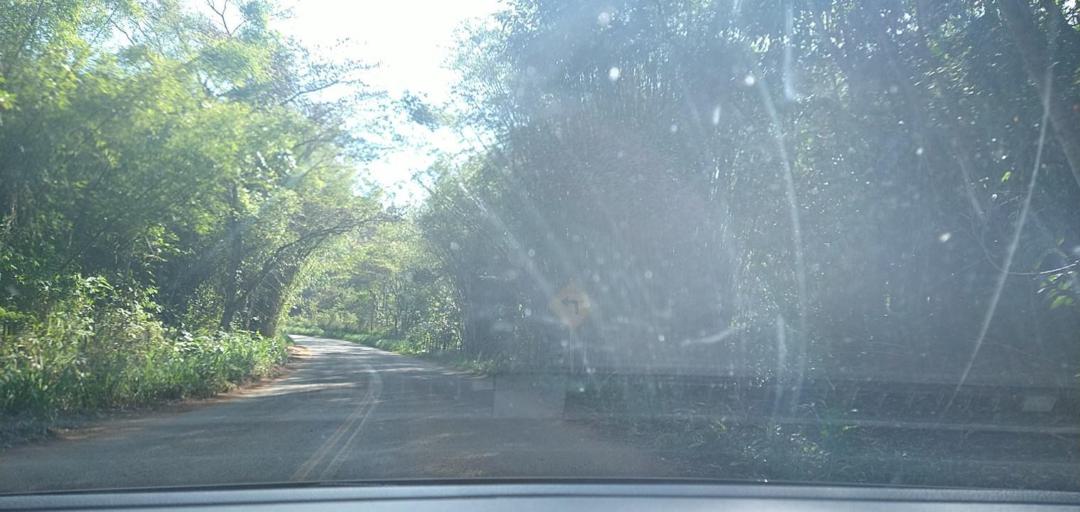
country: BR
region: Minas Gerais
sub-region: Alvinopolis
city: Alvinopolis
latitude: -20.1765
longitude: -42.9295
